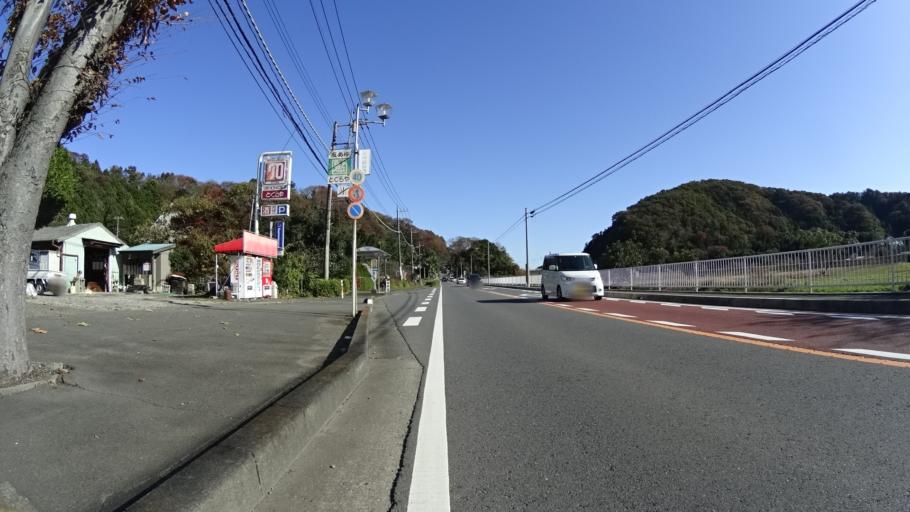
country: JP
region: Kanagawa
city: Zama
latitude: 35.5277
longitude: 139.2989
